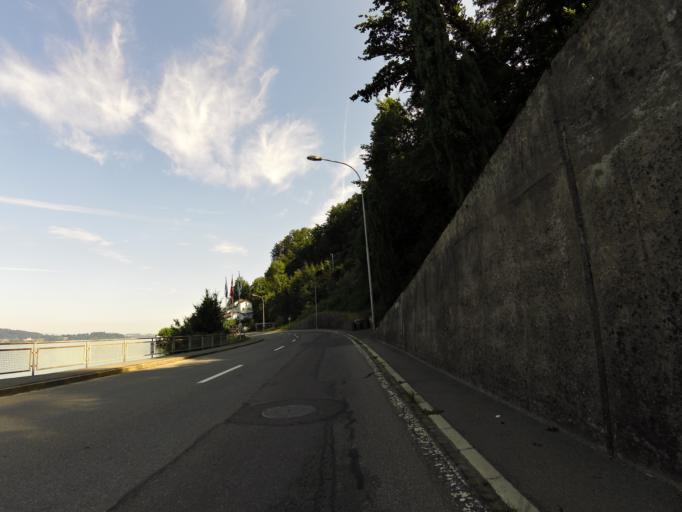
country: CH
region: Zug
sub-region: Zug
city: Walchwil
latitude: 47.1104
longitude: 8.5027
